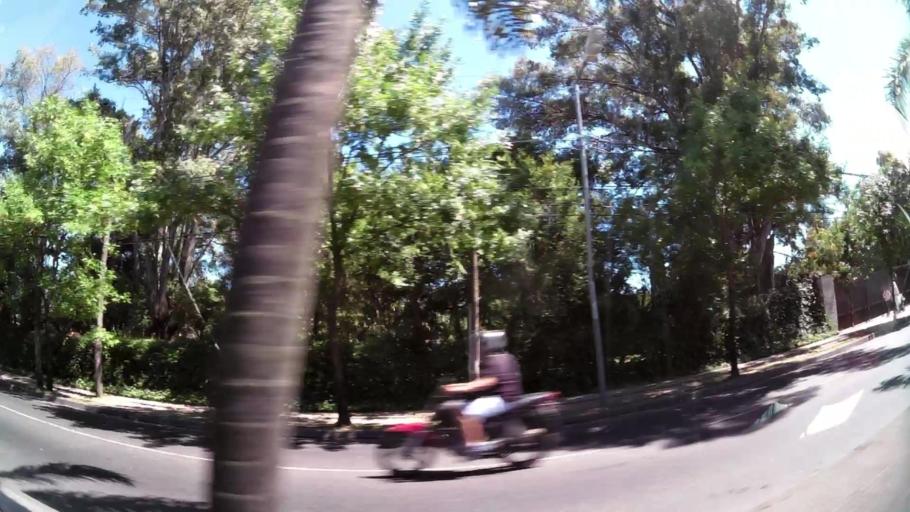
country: AR
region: Buenos Aires
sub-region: Partido de Tigre
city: Tigre
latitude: -34.4893
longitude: -58.6225
